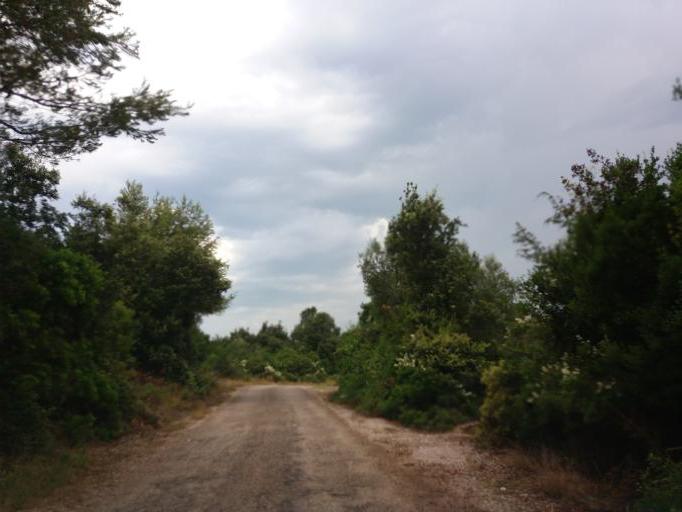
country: HR
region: Zadarska
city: Sali
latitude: 43.9071
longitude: 15.1407
